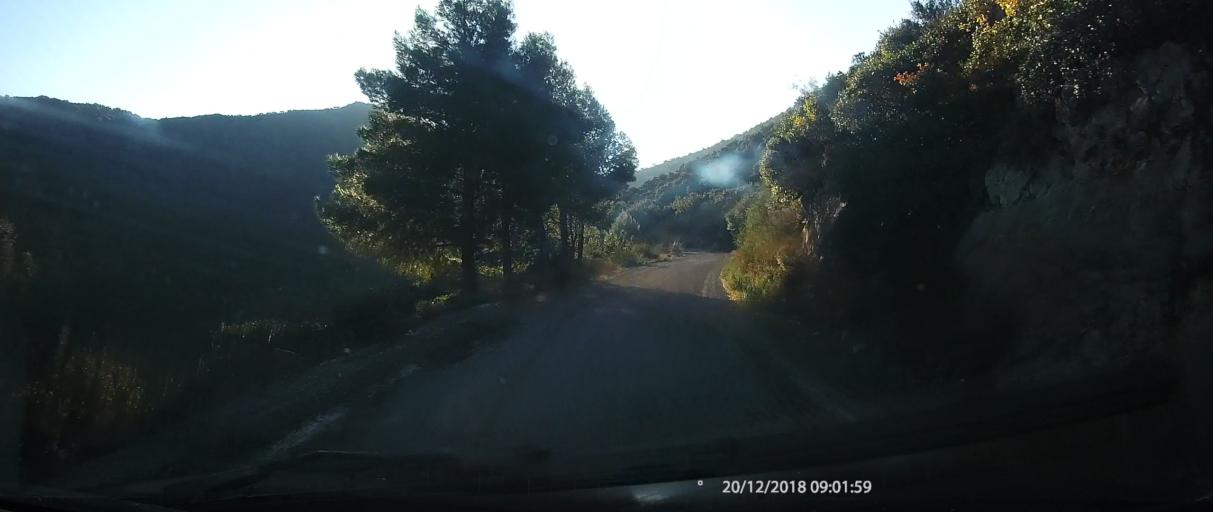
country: GR
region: Peloponnese
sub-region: Nomos Lakonias
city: Sykea
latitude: 36.9566
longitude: 22.9902
